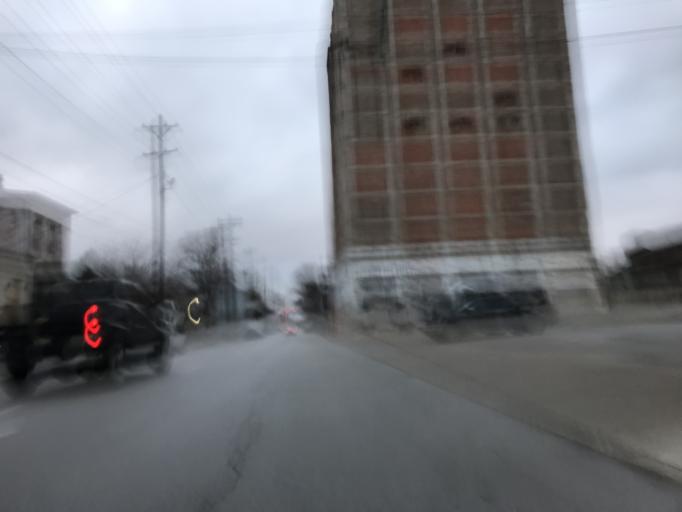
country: US
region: Kentucky
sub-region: Jefferson County
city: Louisville
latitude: 38.2401
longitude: -85.7389
